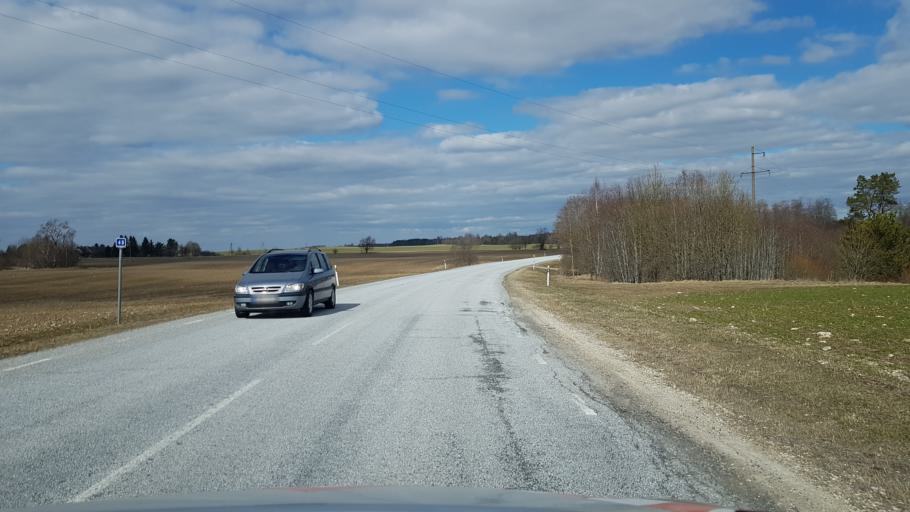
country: EE
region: Laeaene-Virumaa
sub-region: Rakke vald
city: Rakke
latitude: 58.9483
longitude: 26.2717
